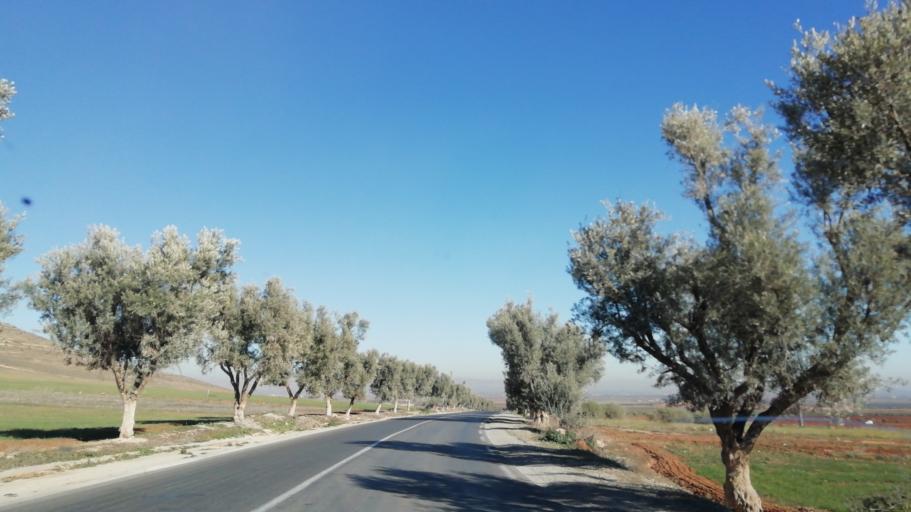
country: DZ
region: Mascara
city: Mascara
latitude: 35.2554
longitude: 0.1252
